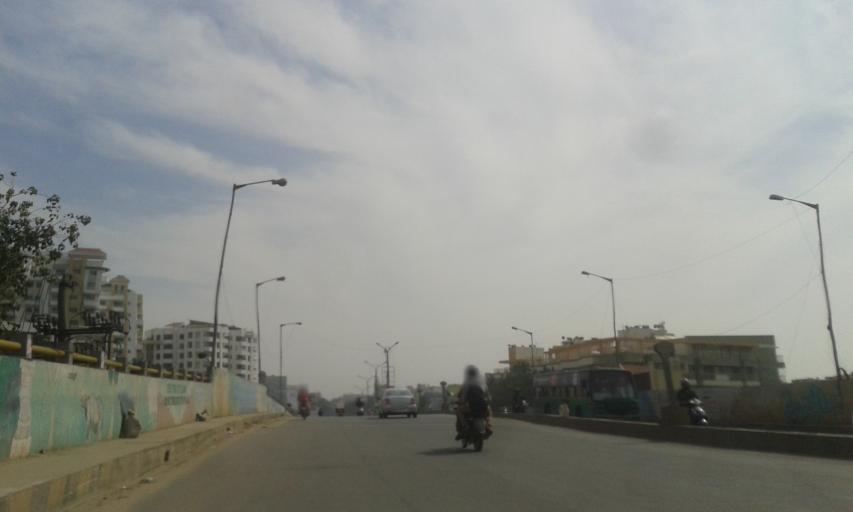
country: IN
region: Karnataka
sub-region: Bangalore Urban
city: Bangalore
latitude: 12.9568
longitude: 77.7042
